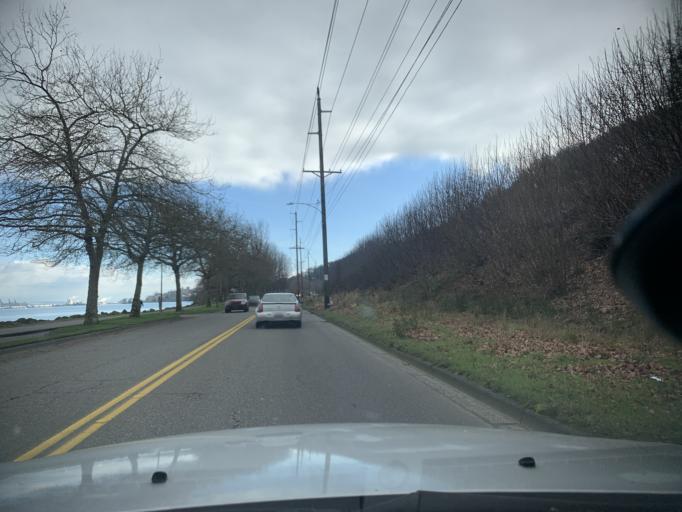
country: US
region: Washington
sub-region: Pierce County
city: Fircrest
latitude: 47.2916
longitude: -122.4943
